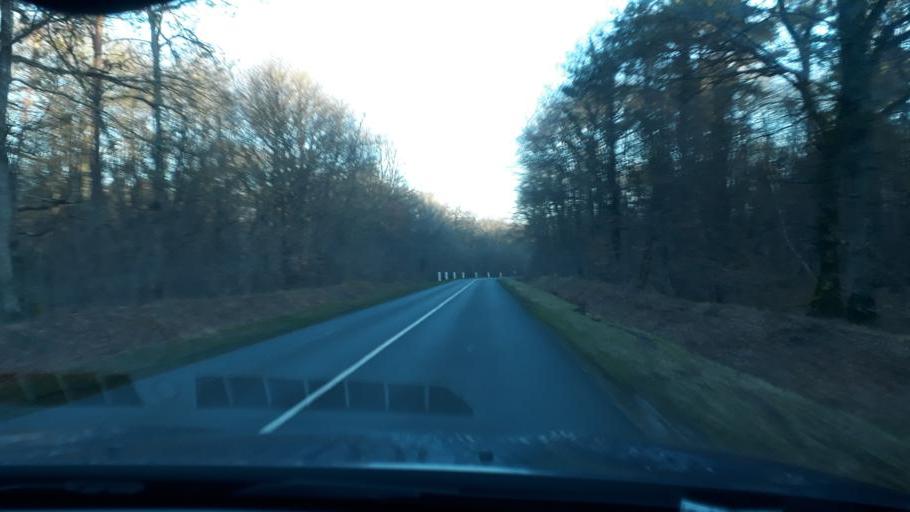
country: FR
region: Centre
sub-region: Departement du Loiret
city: Neuville-aux-Bois
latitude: 48.0372
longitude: 2.0508
